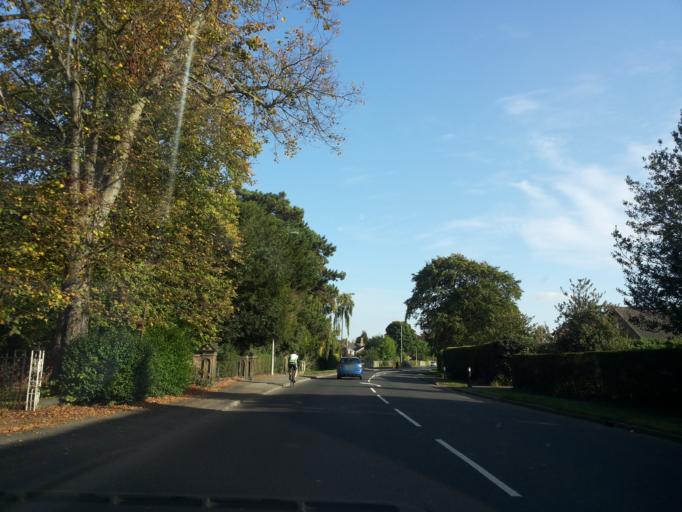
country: GB
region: England
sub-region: East Riding of Yorkshire
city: Snaith
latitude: 53.6911
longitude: -1.0249
